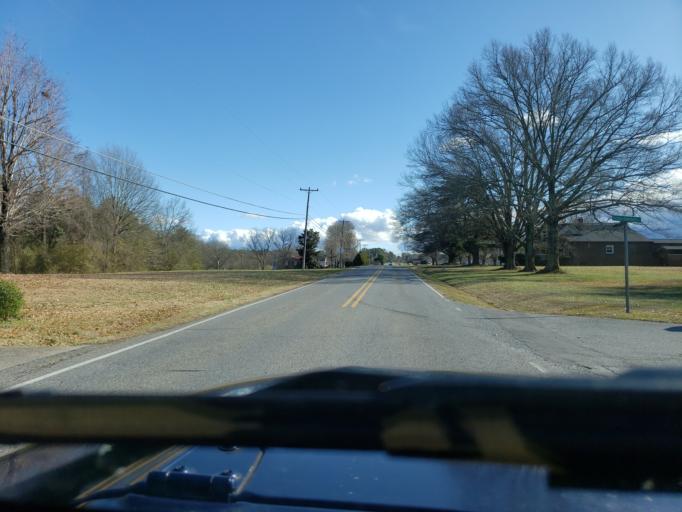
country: US
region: South Carolina
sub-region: Cherokee County
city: Blacksburg
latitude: 35.1877
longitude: -81.4669
